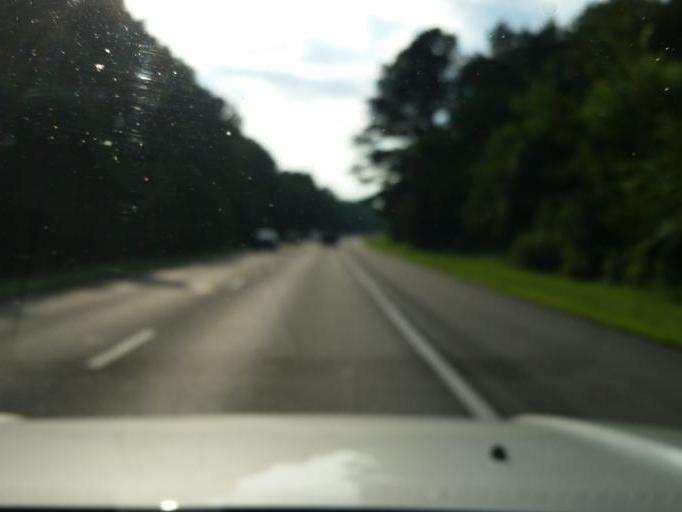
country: US
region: Virginia
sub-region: King William County
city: West Point
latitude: 37.4220
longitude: -76.8263
